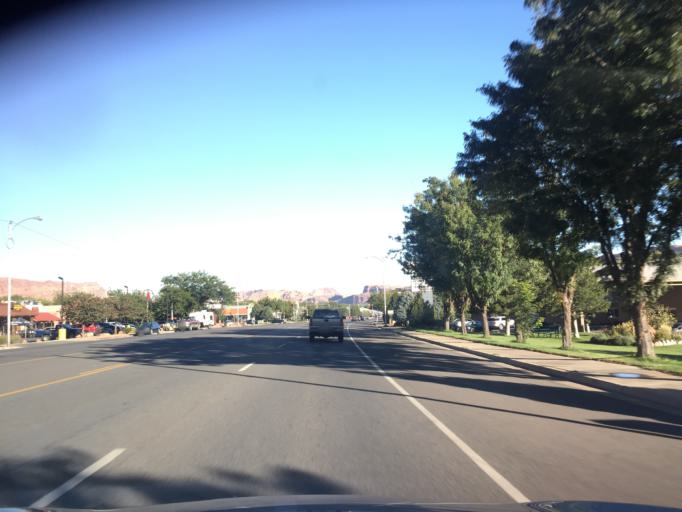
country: US
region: Utah
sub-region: Grand County
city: Moab
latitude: 38.5620
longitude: -109.5483
